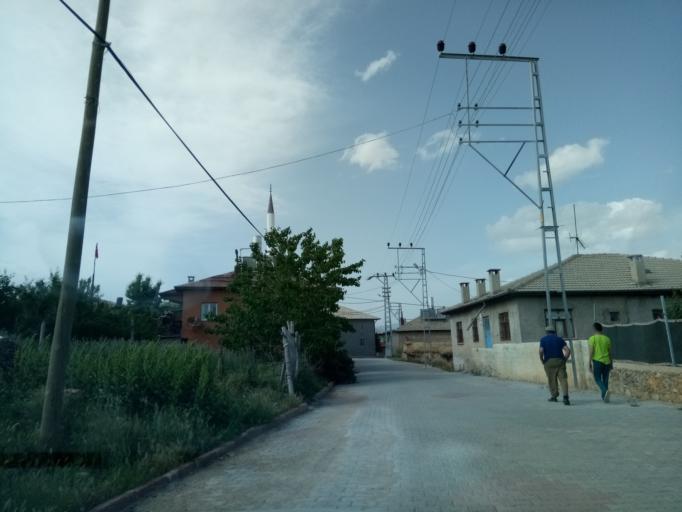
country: TR
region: Konya
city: Ahirli
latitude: 37.2863
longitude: 32.1792
